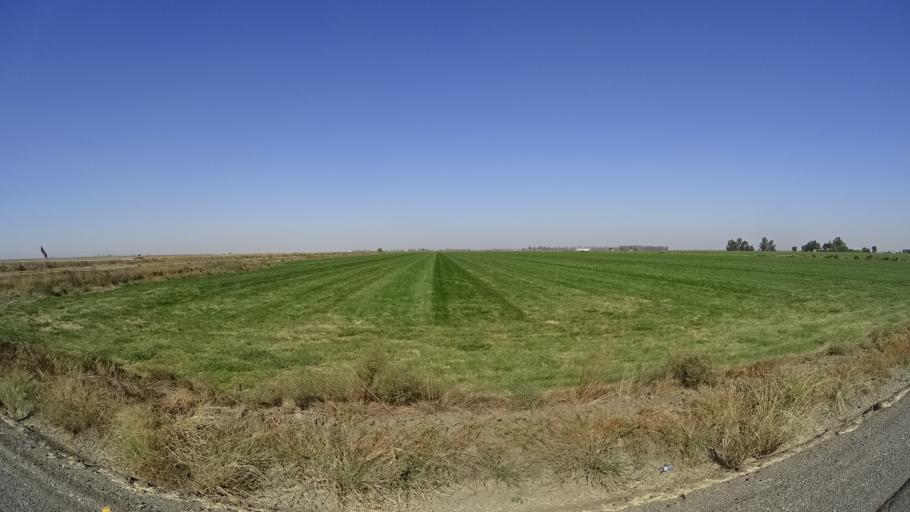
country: US
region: California
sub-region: Yolo County
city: Winters
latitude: 38.5906
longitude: -121.8862
